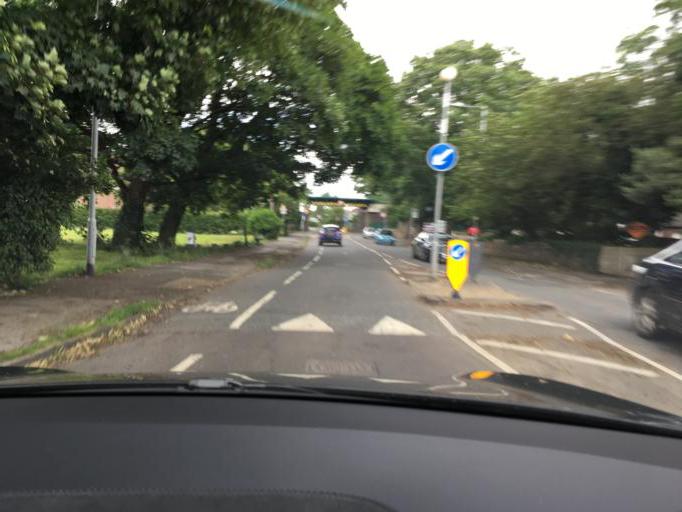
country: GB
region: England
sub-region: Borough of Stockport
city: Hazel Grove
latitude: 53.3746
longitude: -2.1225
